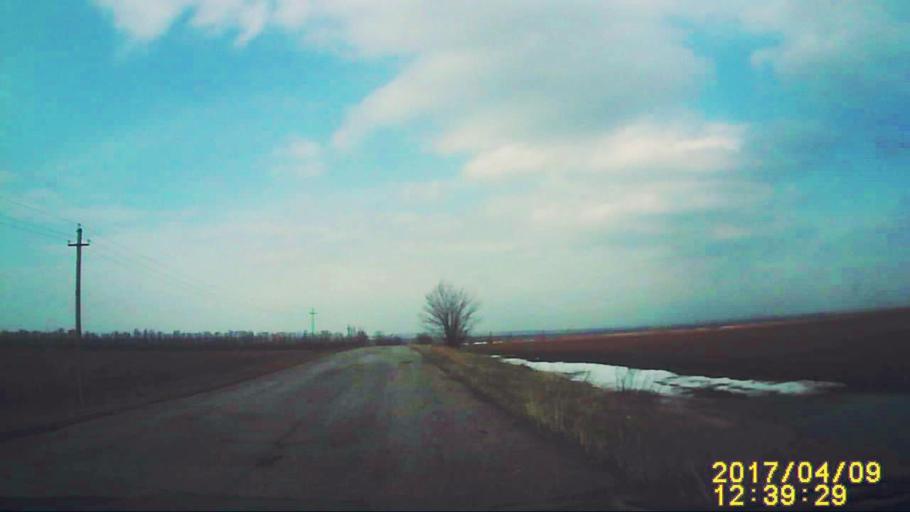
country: RU
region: Ulyanovsk
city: Ignatovka
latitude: 53.9992
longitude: 47.9560
